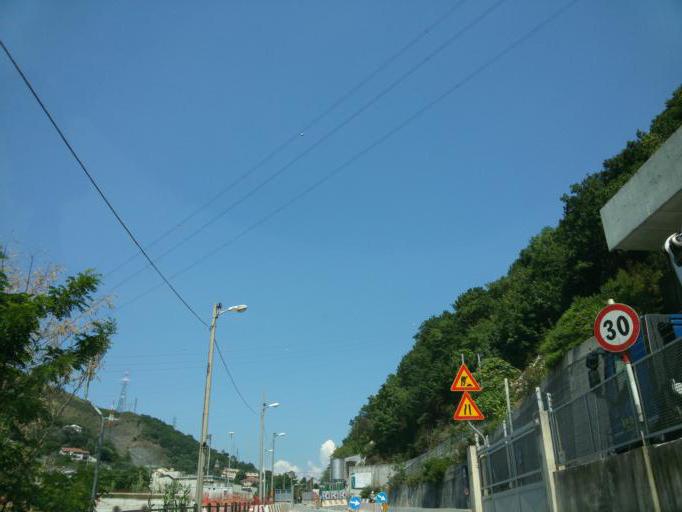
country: IT
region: Liguria
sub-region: Provincia di Genova
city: San Teodoro
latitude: 44.4313
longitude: 8.8615
